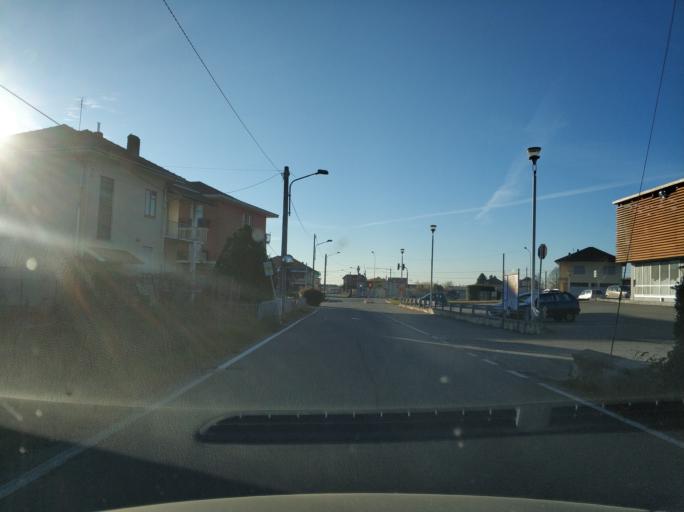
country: IT
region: Piedmont
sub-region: Provincia di Torino
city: Grosso
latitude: 45.2503
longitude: 7.5562
